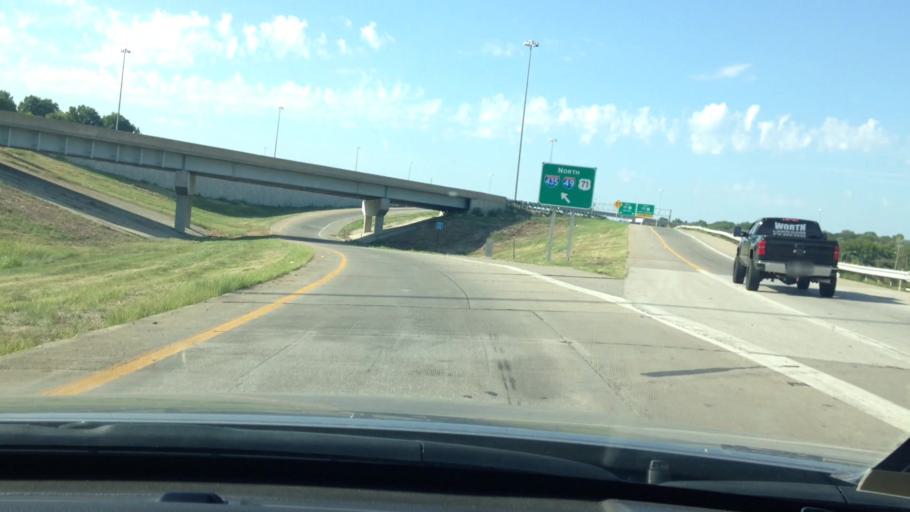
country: US
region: Missouri
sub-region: Jackson County
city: Grandview
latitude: 38.9259
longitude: -94.5265
